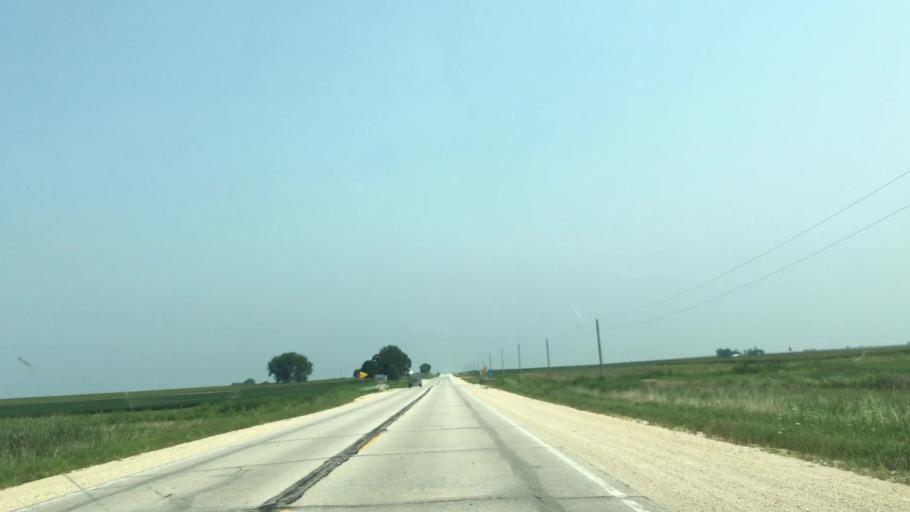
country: US
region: Iowa
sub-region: Fayette County
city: Oelwein
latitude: 42.6873
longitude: -91.8097
